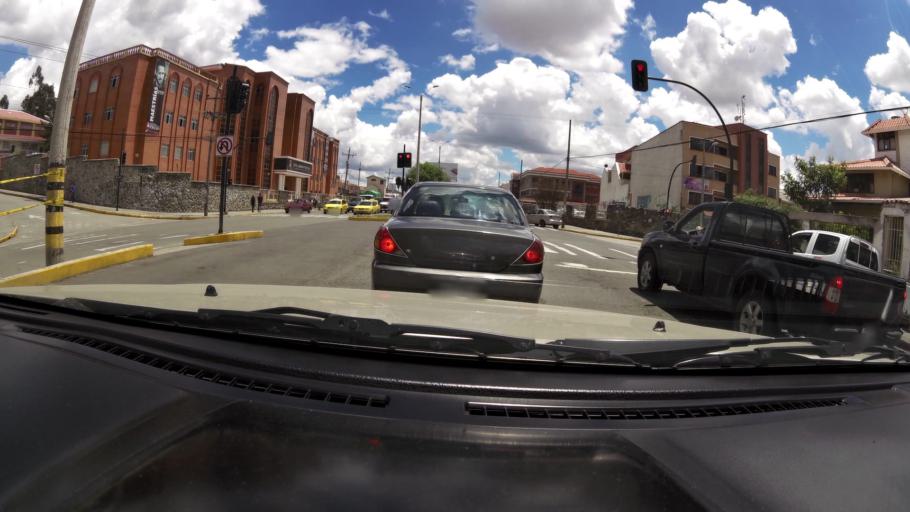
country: EC
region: Azuay
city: Cuenca
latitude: -2.8852
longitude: -79.0068
